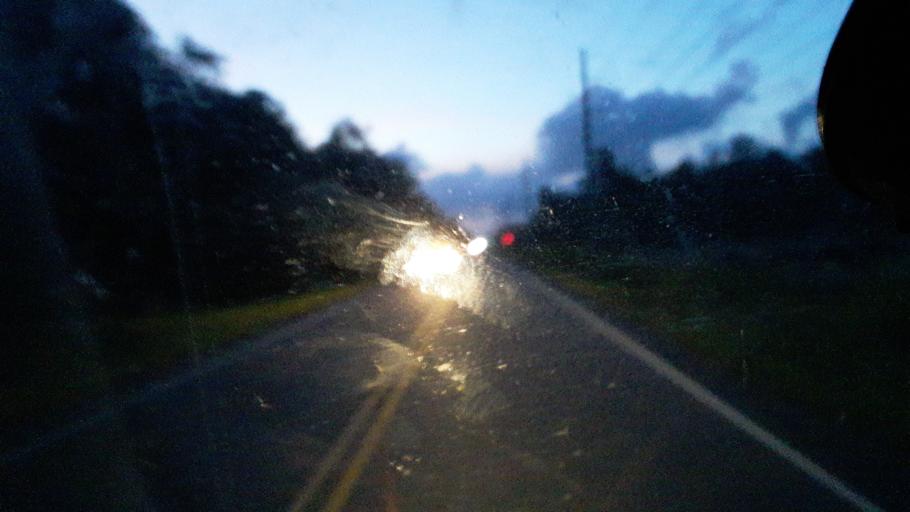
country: US
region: North Carolina
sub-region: Brunswick County
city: Oak Island
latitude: 33.9916
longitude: -78.2125
